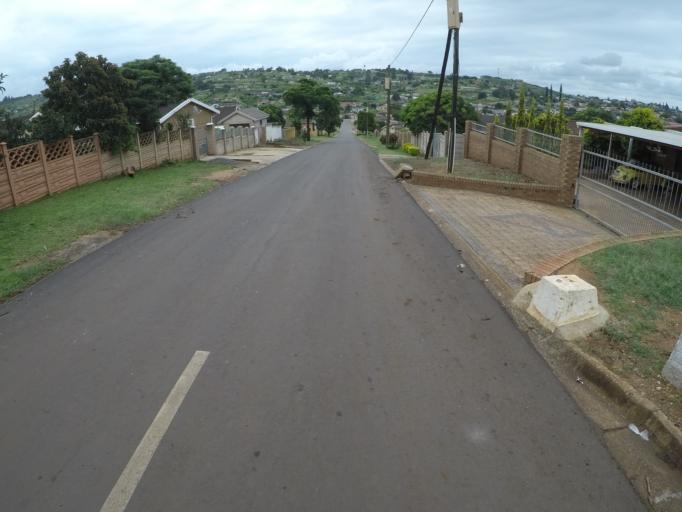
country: ZA
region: KwaZulu-Natal
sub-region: uThungulu District Municipality
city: Empangeni
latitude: -28.7767
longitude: 31.8504
